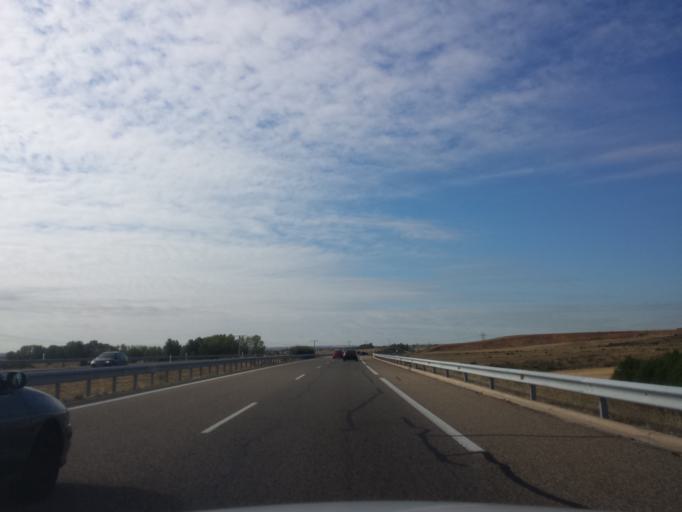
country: ES
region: Castille and Leon
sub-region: Provincia de Leon
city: Ardon
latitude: 42.4618
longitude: -5.5824
